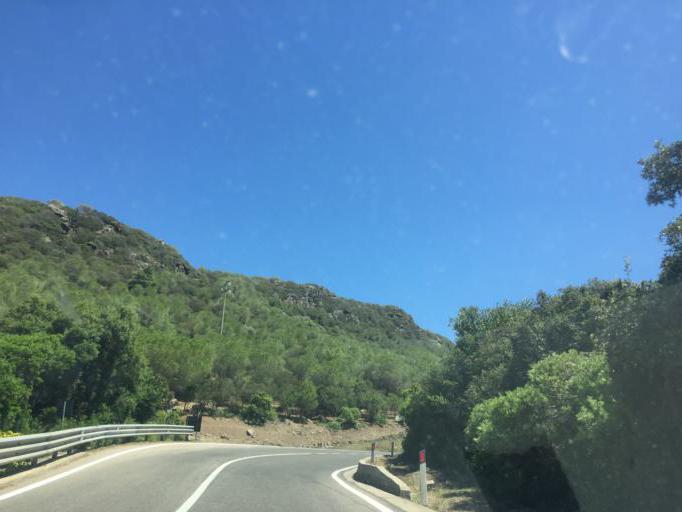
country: IT
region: Sardinia
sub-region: Provincia di Sassari
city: Castelsardo
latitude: 40.9009
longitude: 8.7409
